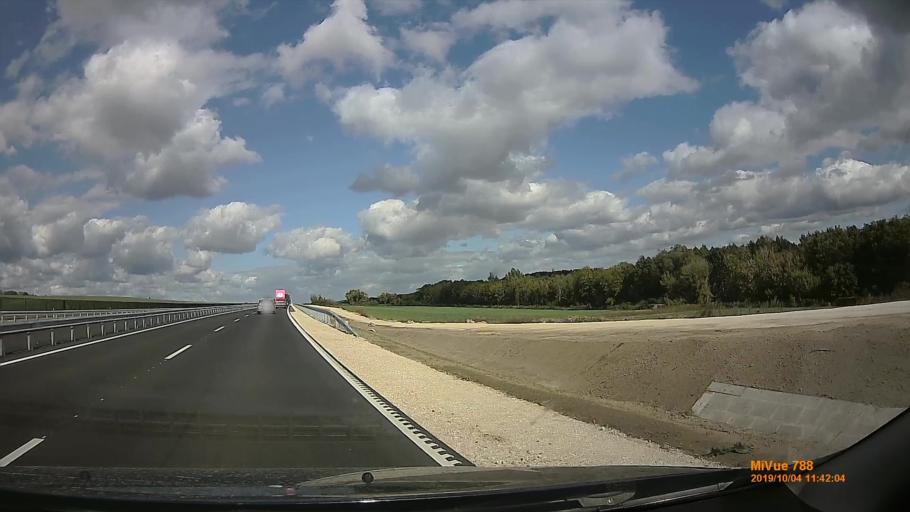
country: HU
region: Somogy
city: Karad
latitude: 46.5854
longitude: 17.8036
